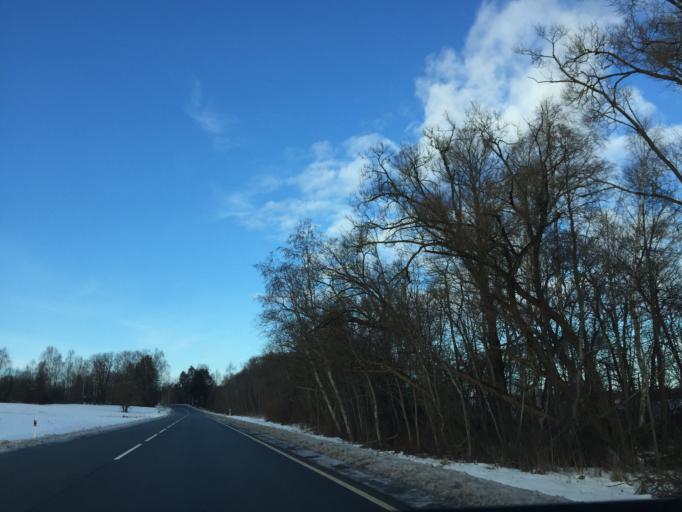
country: LV
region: Ogre
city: Jumprava
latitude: 56.6505
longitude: 24.8802
